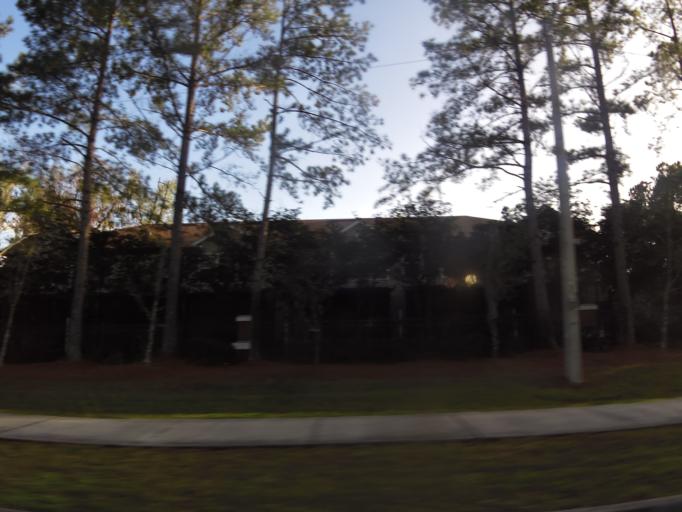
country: US
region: Florida
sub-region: Duval County
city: Jacksonville
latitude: 30.2696
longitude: -81.5648
